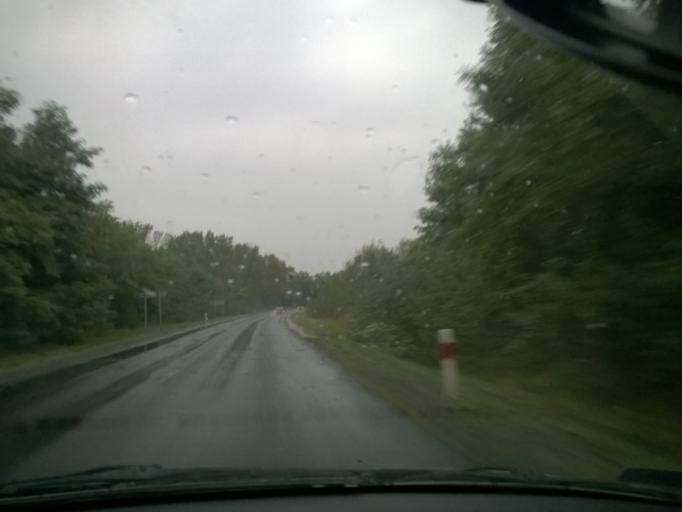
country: HU
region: Pest
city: Domsod
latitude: 47.1280
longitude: 18.9980
